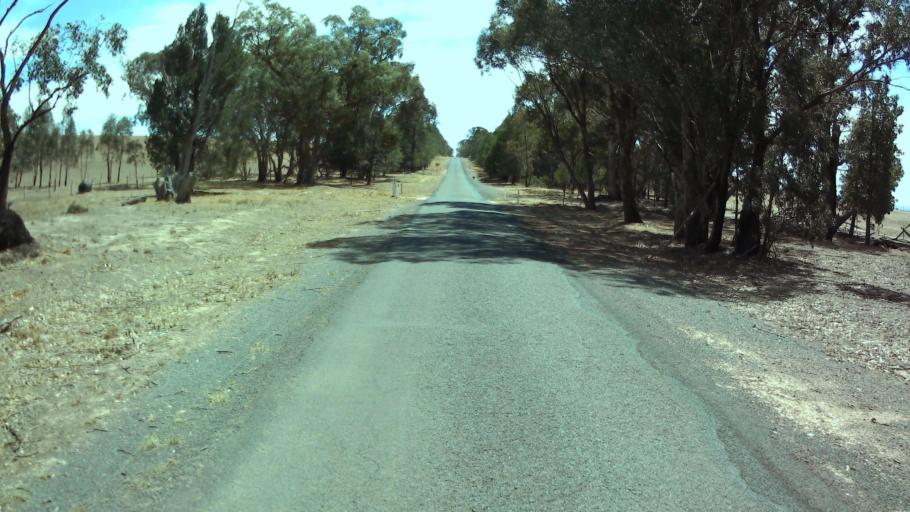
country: AU
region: New South Wales
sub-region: Weddin
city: Grenfell
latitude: -33.7628
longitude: 148.2048
